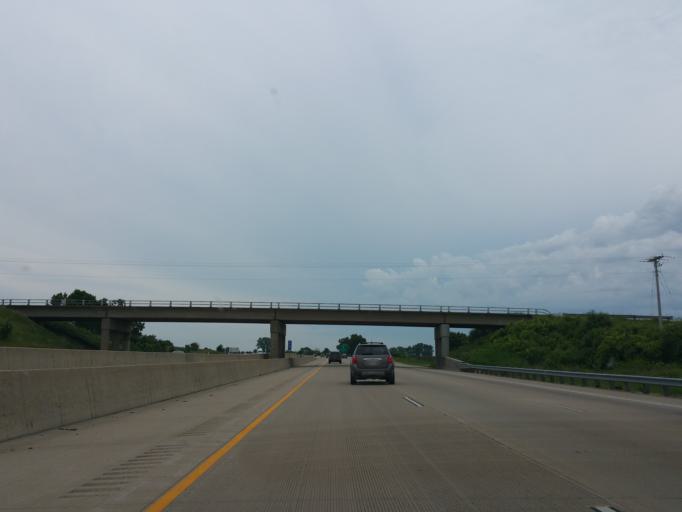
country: US
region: Wisconsin
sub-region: Columbia County
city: Poynette
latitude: 43.3535
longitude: -89.4598
